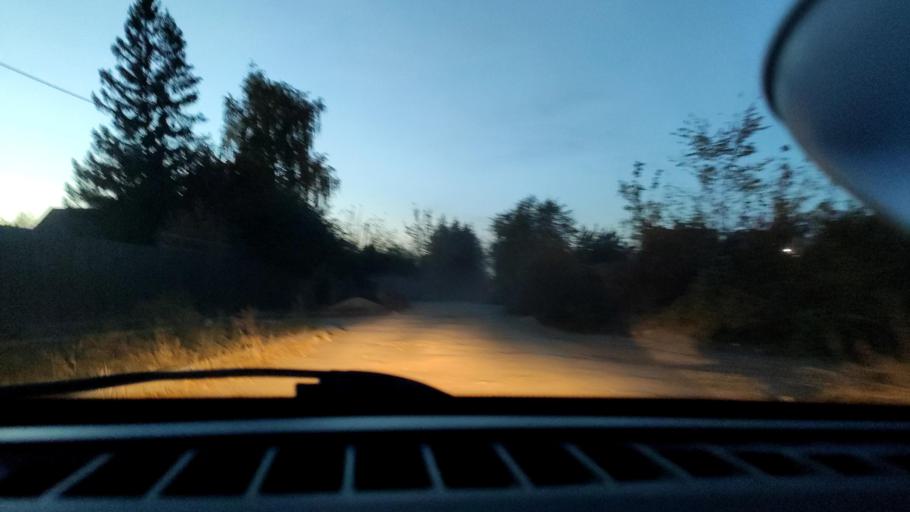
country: RU
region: Samara
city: Samara
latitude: 53.2202
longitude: 50.2175
